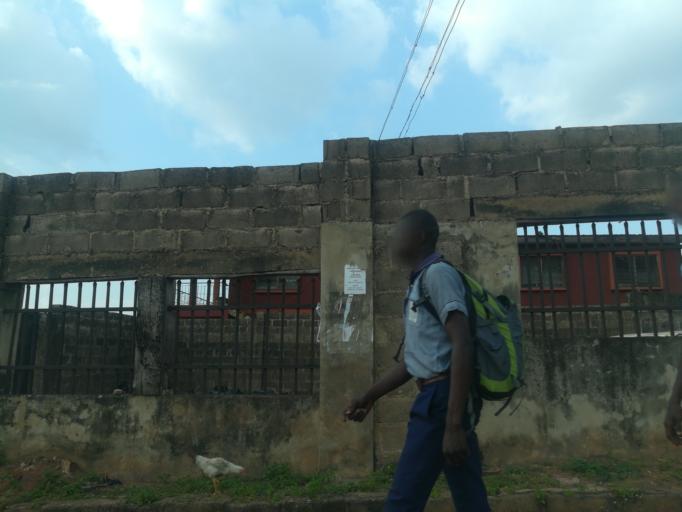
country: NG
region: Oyo
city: Moniya
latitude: 7.4805
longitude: 3.9127
